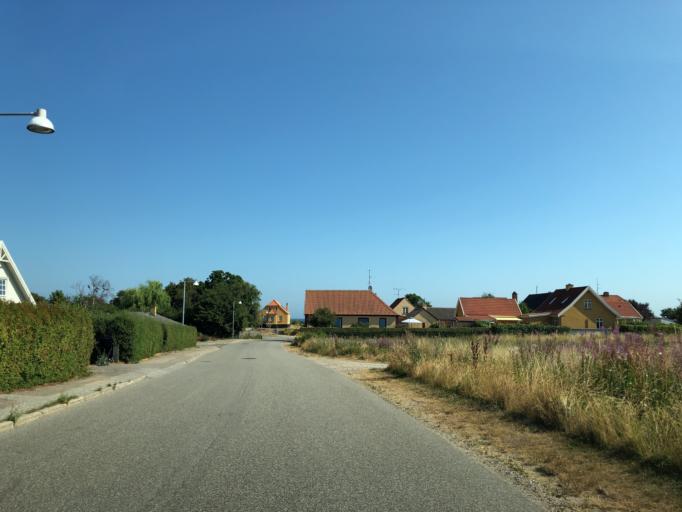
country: DK
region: Zealand
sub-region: Odsherred Kommune
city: Asnaes
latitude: 55.9720
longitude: 11.3597
